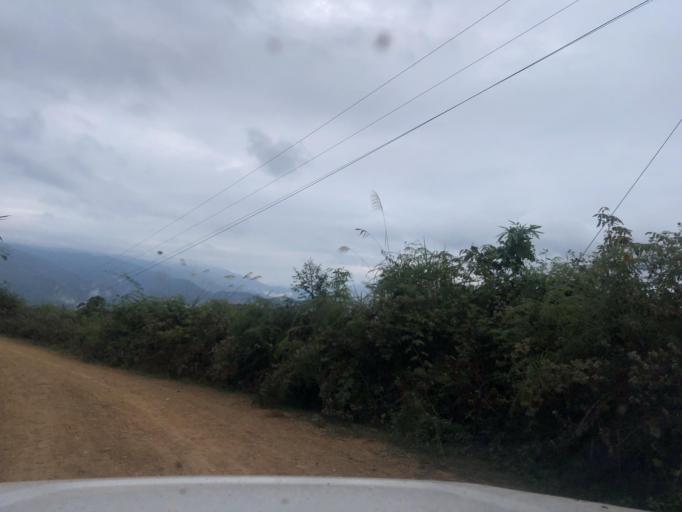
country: LA
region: Phongsali
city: Khoa
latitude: 21.2661
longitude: 102.5876
